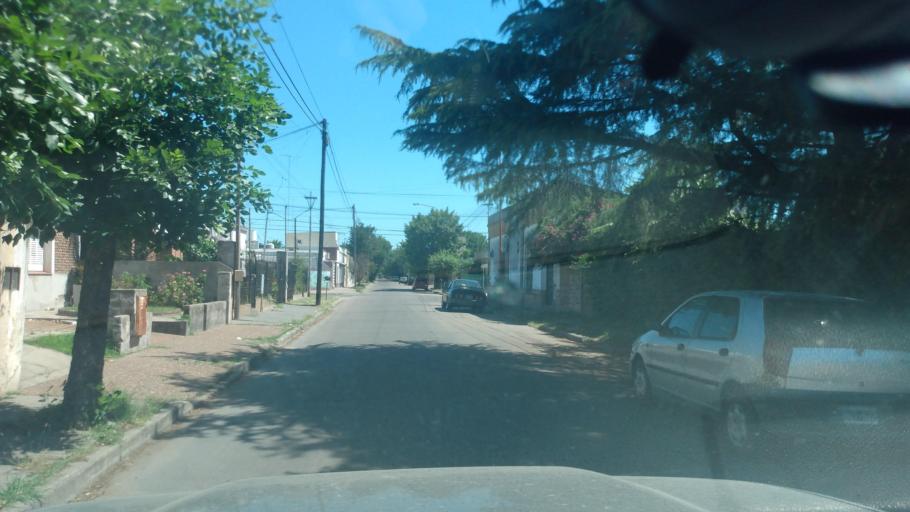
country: AR
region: Buenos Aires
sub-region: Partido de Lujan
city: Lujan
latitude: -34.5647
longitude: -59.1047
